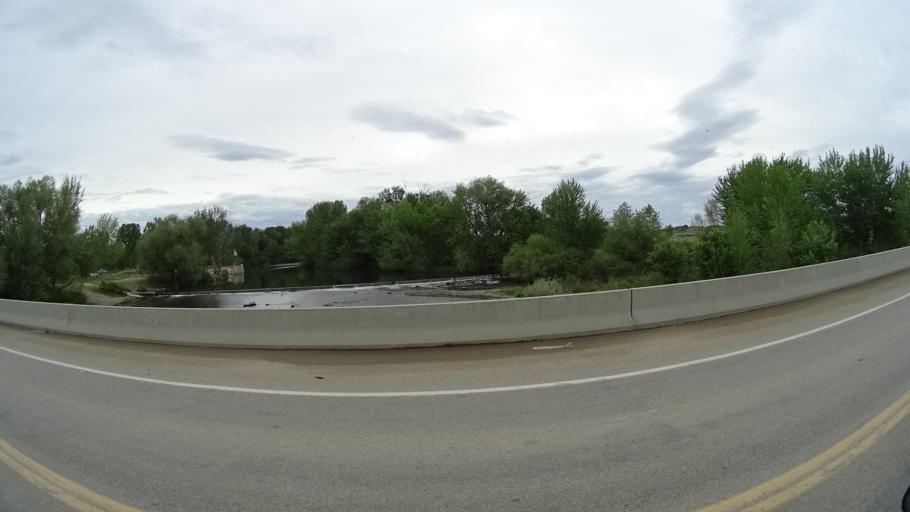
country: US
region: Idaho
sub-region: Ada County
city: Star
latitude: 43.6805
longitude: -116.4932
